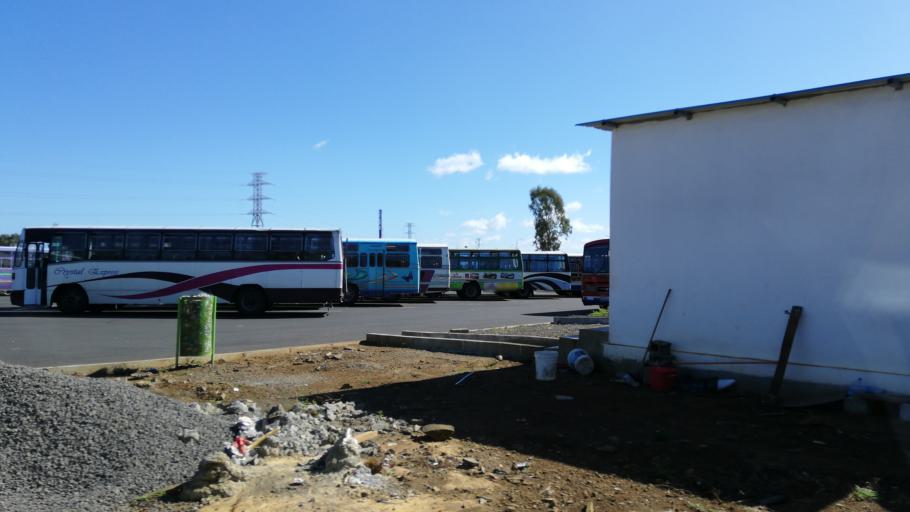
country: MU
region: Plaines Wilhems
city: Ebene
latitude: -20.2406
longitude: 57.4803
